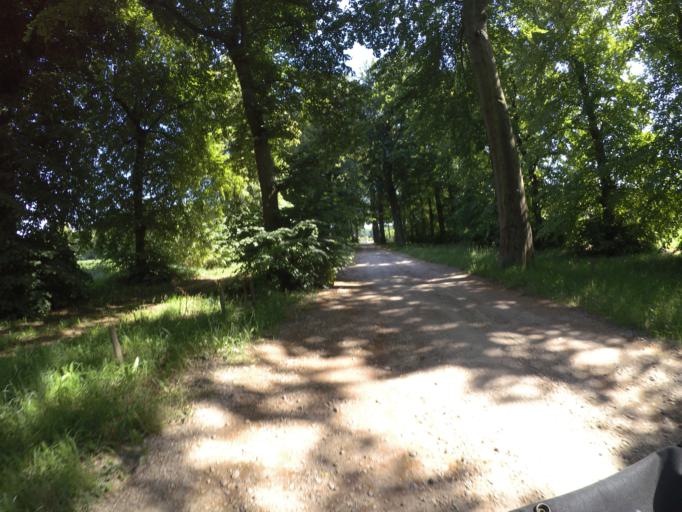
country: NL
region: North Brabant
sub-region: Gemeente Heusden
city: Heusden
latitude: 51.6904
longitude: 5.1706
